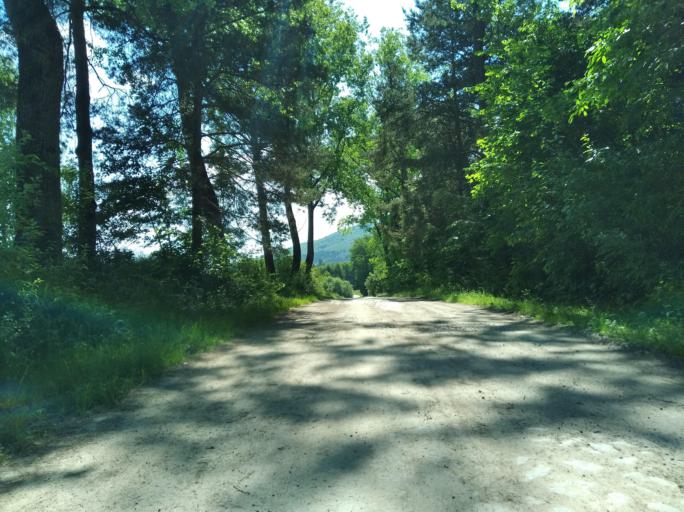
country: PL
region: Subcarpathian Voivodeship
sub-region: Powiat krosnienski
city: Odrzykon
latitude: 49.7676
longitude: 21.7799
